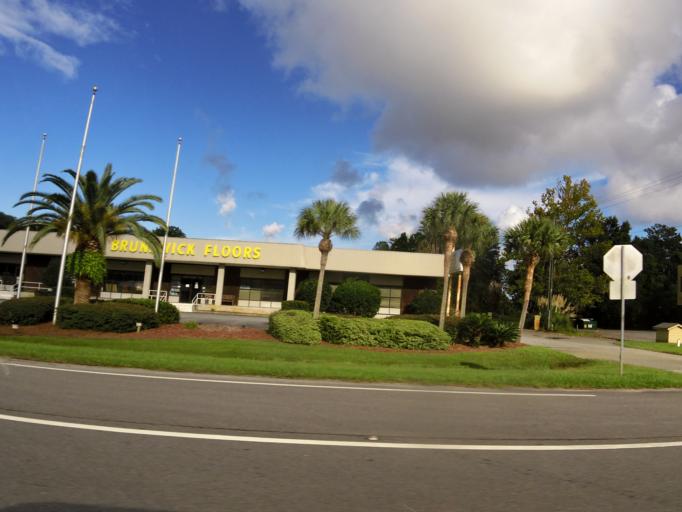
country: US
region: Georgia
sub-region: Glynn County
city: Country Club Estates
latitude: 31.1882
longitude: -81.4694
